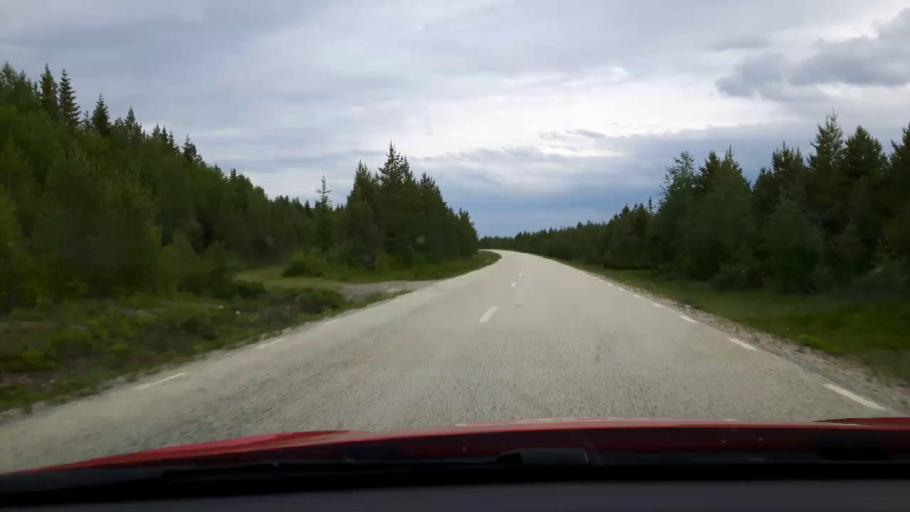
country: SE
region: Jaemtland
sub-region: Bergs Kommun
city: Hoverberg
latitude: 62.7079
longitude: 13.9363
